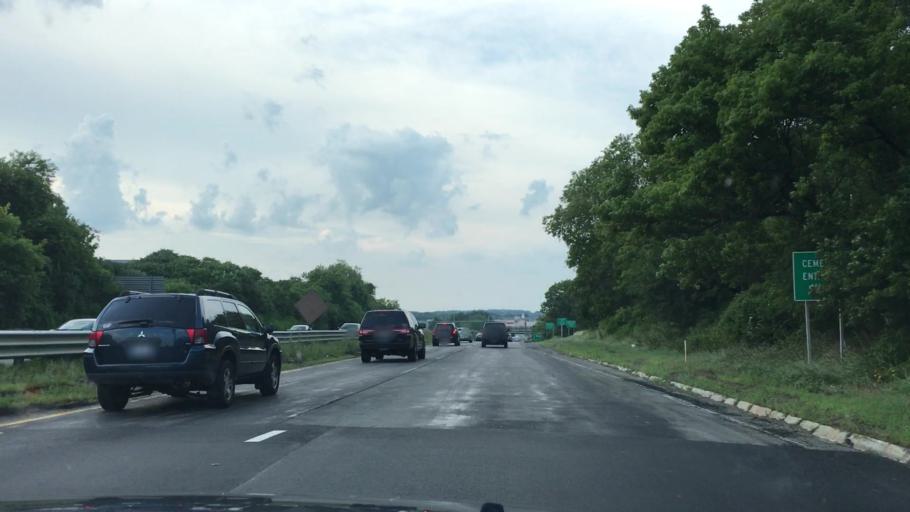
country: US
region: Massachusetts
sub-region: Essex County
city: Peabody
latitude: 42.5437
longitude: -70.9359
